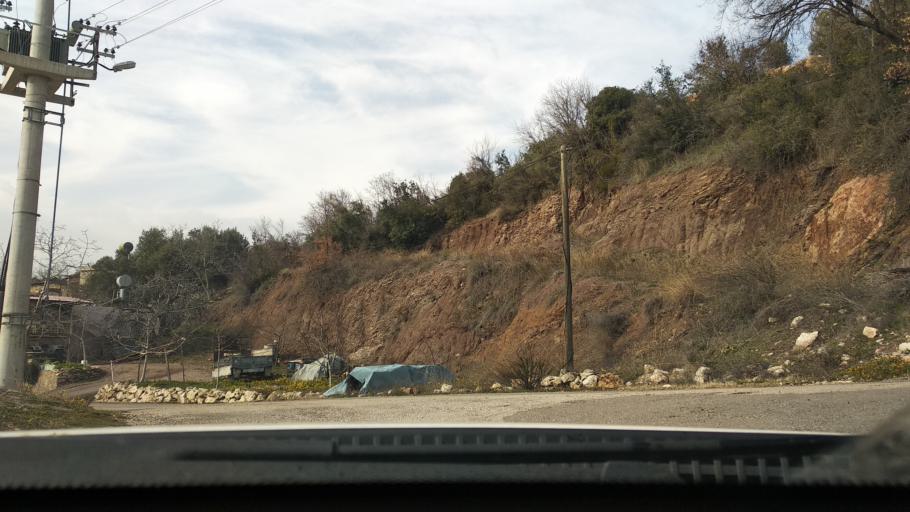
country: TR
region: Mersin
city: Kuzucubelen
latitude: 36.8778
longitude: 34.4681
